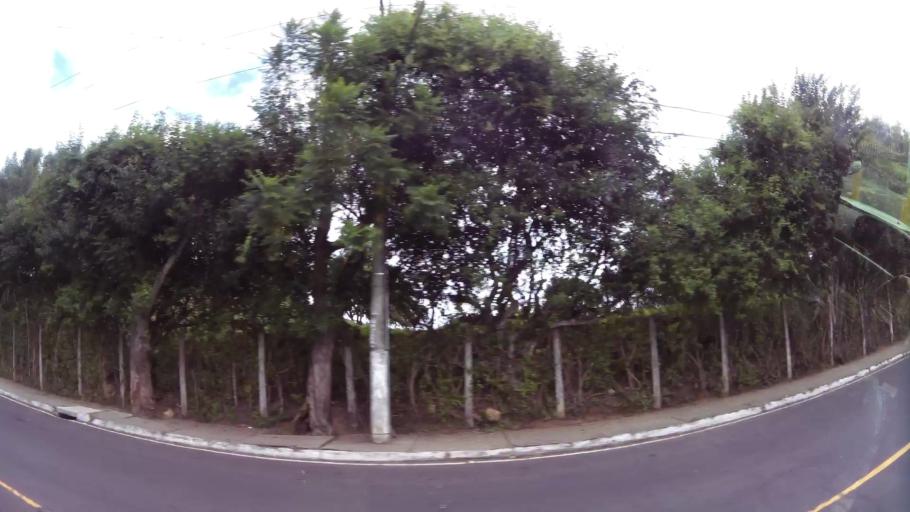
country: GT
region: Guatemala
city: Guatemala City
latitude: 14.6320
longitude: -90.5492
